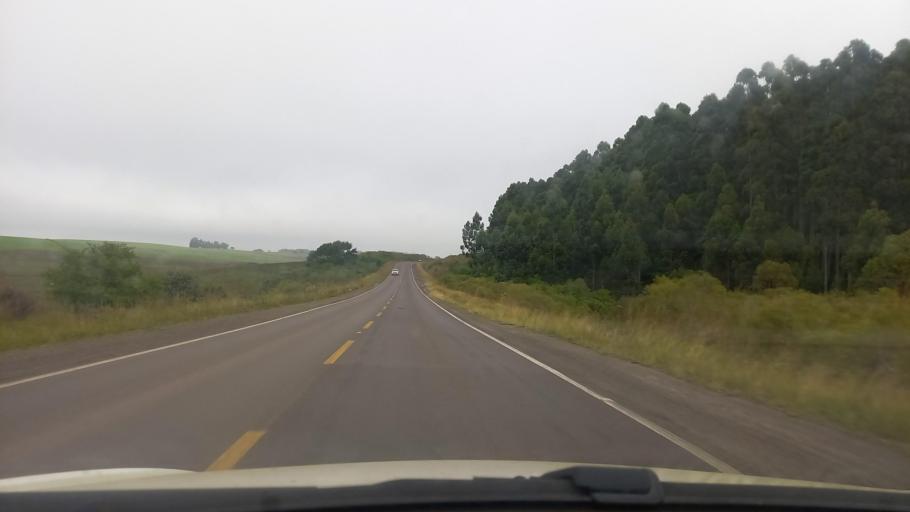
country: BR
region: Rio Grande do Sul
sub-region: Rosario Do Sul
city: Rosario do Sul
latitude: -30.1743
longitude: -54.6955
